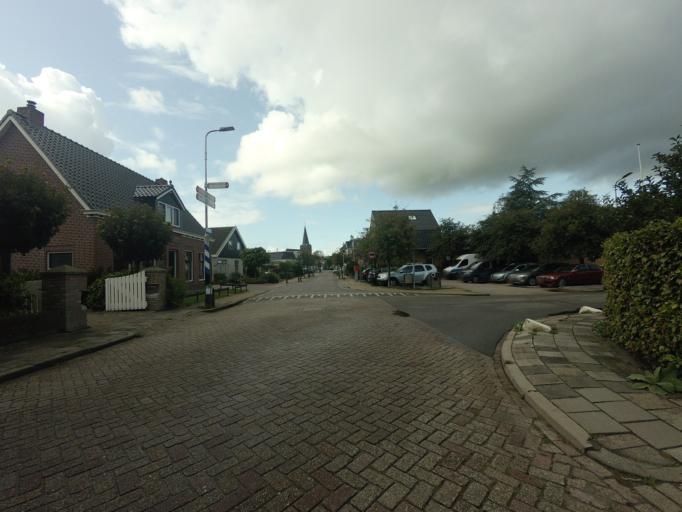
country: NL
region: Friesland
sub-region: Gemeente Boarnsterhim
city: Warten
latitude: 53.1505
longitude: 5.8993
